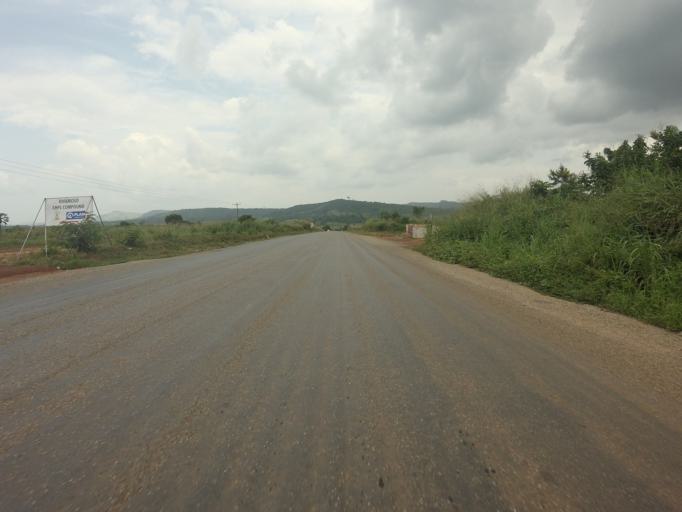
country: GH
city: Akropong
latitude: 5.9594
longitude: -0.1419
